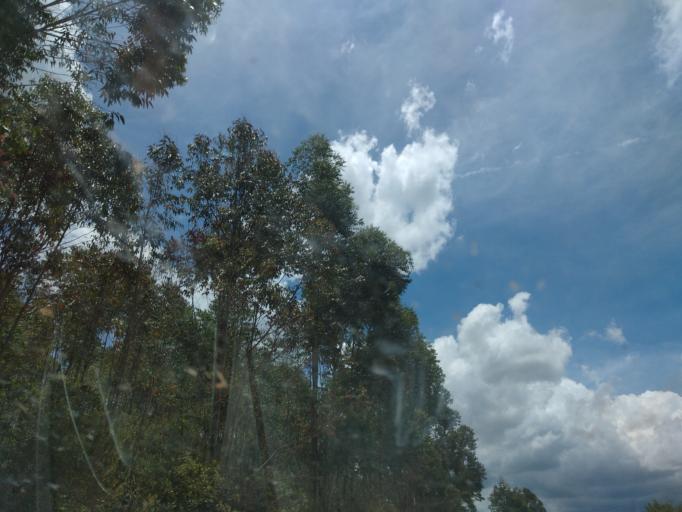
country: BR
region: Minas Gerais
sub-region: Sao Joao Del Rei
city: Sao Joao del Rei
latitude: -20.8960
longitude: -44.3040
